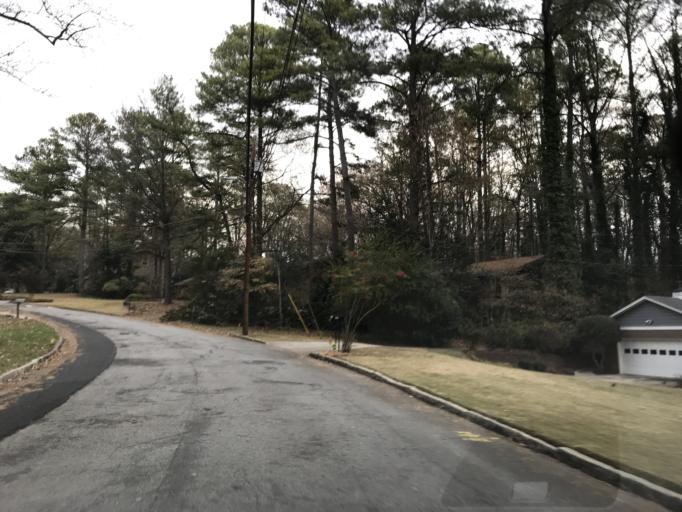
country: US
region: Georgia
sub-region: DeKalb County
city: Doraville
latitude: 33.8807
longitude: -84.2544
